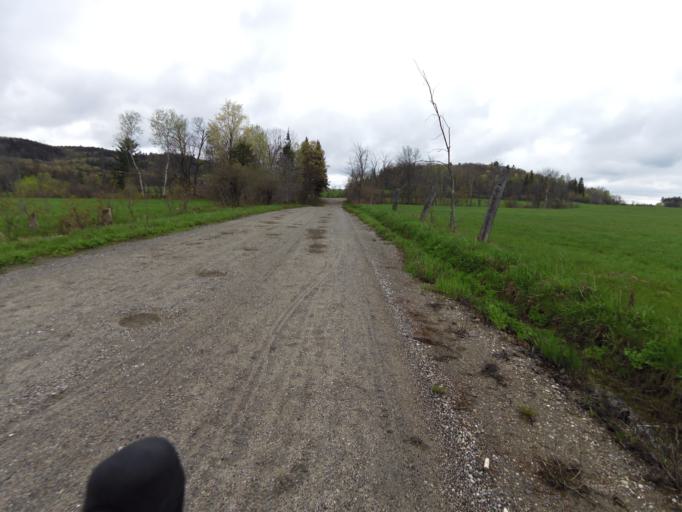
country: CA
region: Quebec
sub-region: Outaouais
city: Wakefield
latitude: 45.5854
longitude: -75.9021
